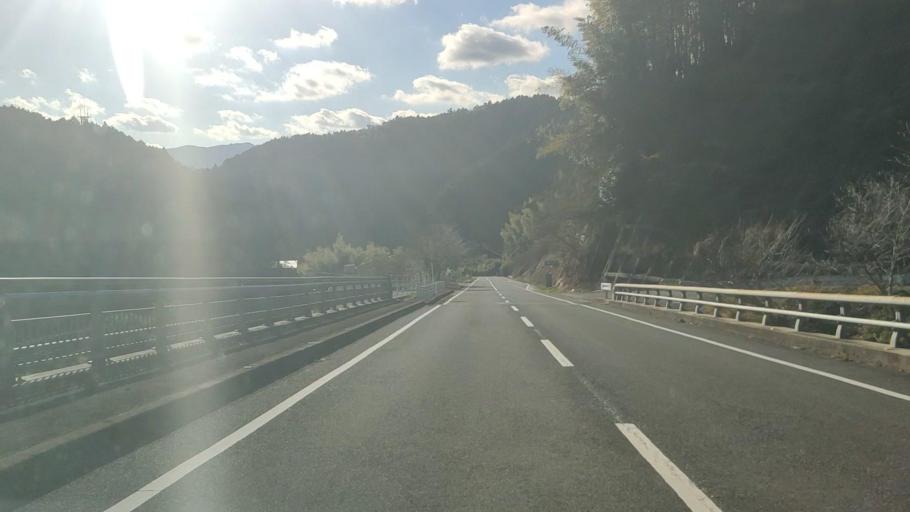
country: JP
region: Saga Prefecture
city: Kanzakimachi-kanzaki
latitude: 33.3891
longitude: 130.2648
